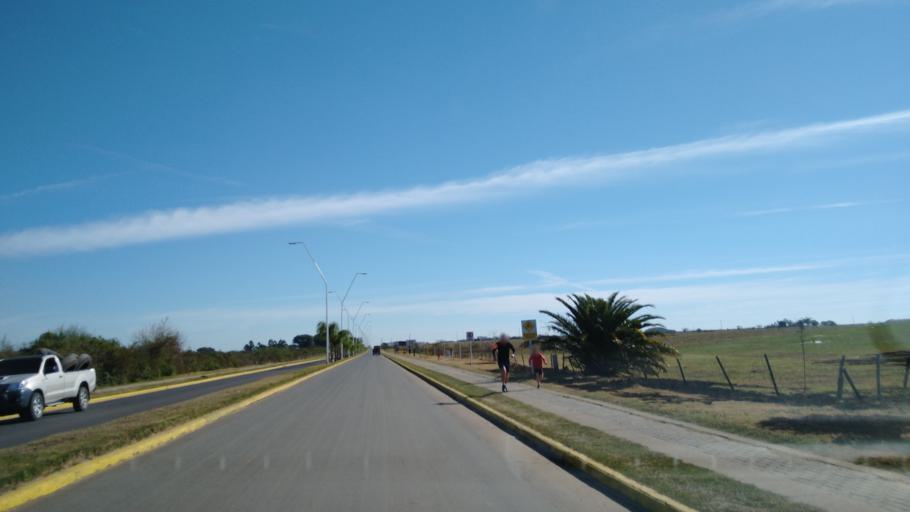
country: AR
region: Entre Rios
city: Chajari
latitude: -30.7582
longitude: -57.9999
